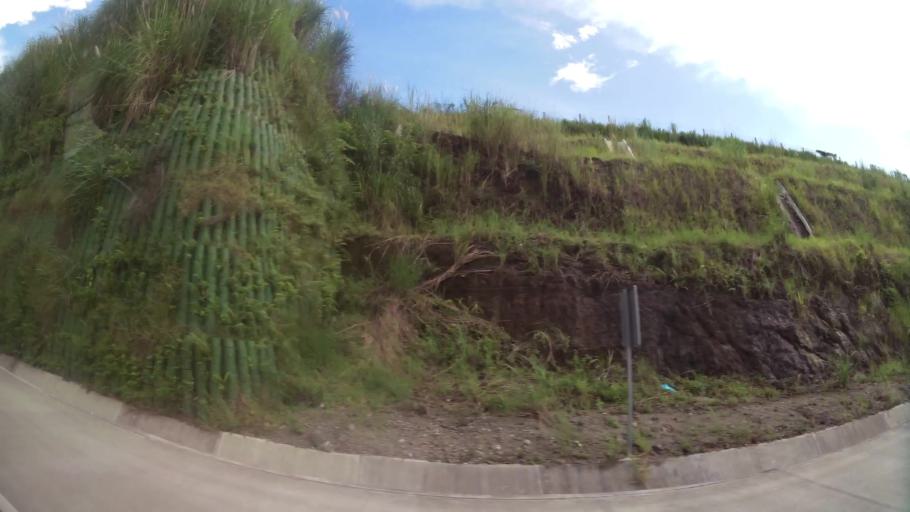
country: PA
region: Panama
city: San Miguelito
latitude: 9.0803
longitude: -79.4541
